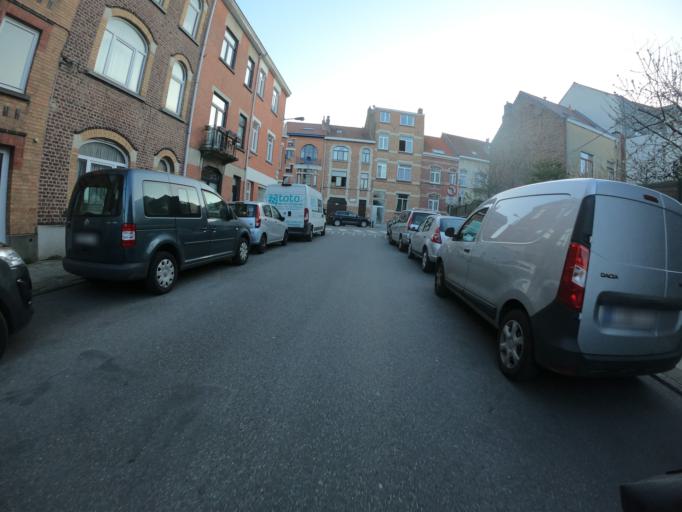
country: BE
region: Flanders
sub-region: Provincie Vlaams-Brabant
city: Kraainem
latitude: 50.8465
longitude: 4.4230
